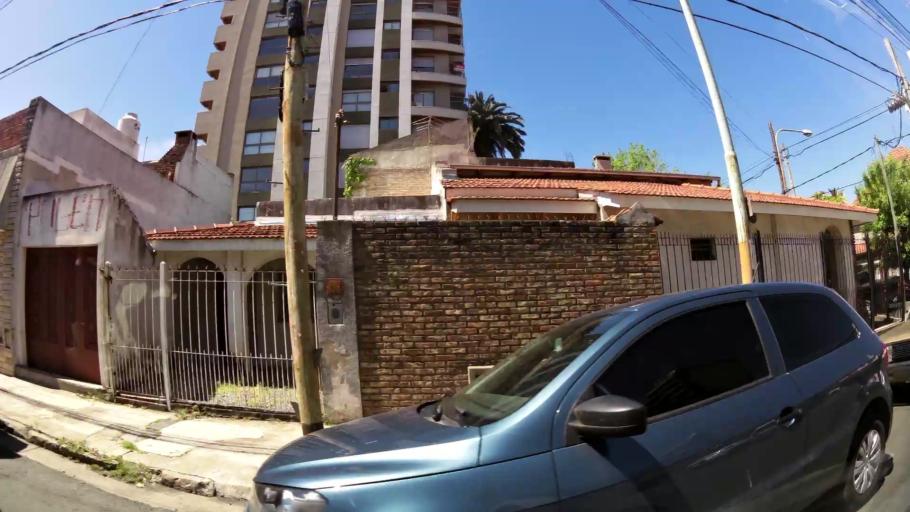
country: AR
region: Buenos Aires
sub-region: Partido de Quilmes
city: Quilmes
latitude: -34.7232
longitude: -58.2512
